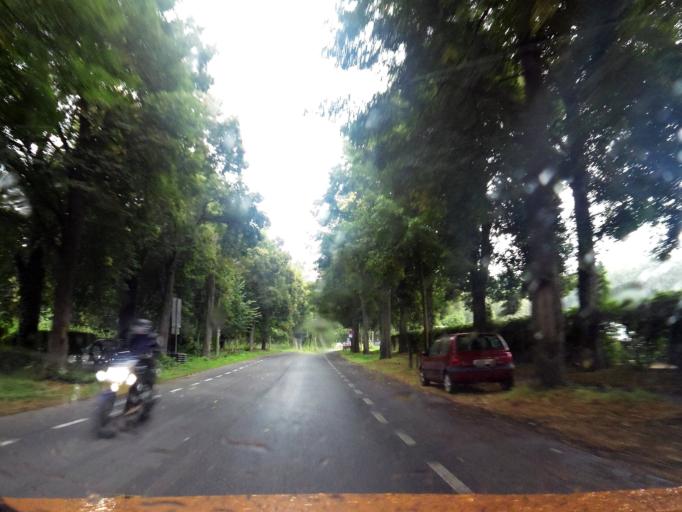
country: DE
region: Brandenburg
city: Potsdam
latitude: 52.4068
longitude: 13.0138
